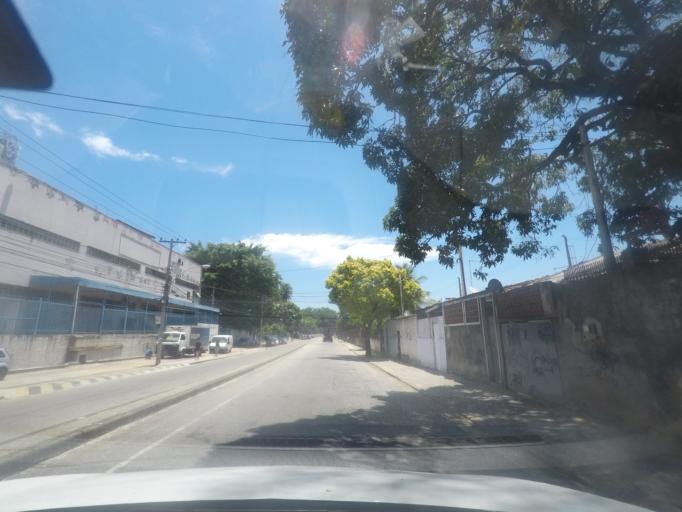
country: BR
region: Rio de Janeiro
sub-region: Itaguai
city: Itaguai
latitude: -22.9172
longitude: -43.6862
